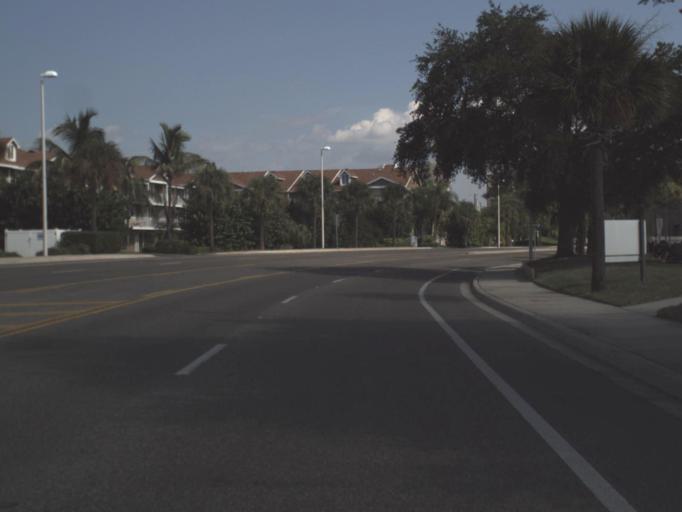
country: US
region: Florida
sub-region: Pinellas County
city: Treasure Island
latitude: 27.7536
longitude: -82.7576
